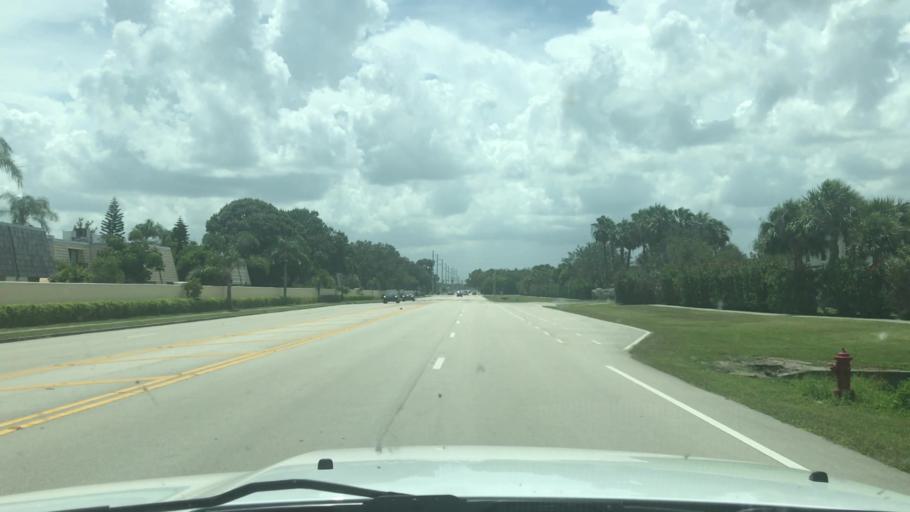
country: US
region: Florida
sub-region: Indian River County
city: Vero Beach
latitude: 27.6234
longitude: -80.3815
